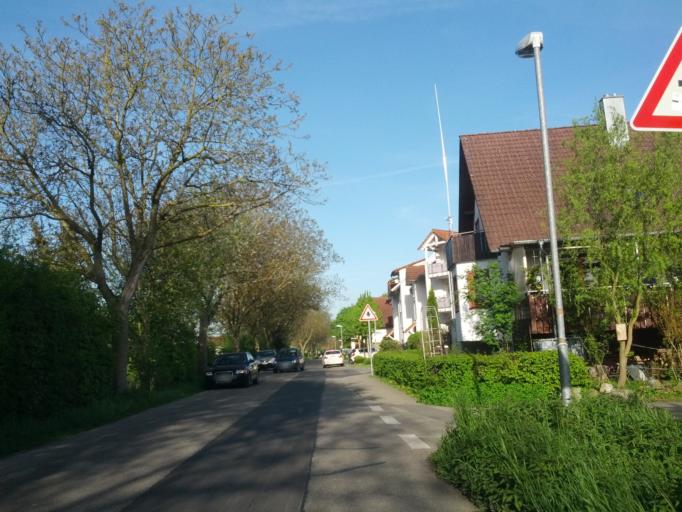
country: DE
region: Baden-Wuerttemberg
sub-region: Freiburg Region
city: Eichstetten
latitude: 48.1063
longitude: 7.7689
